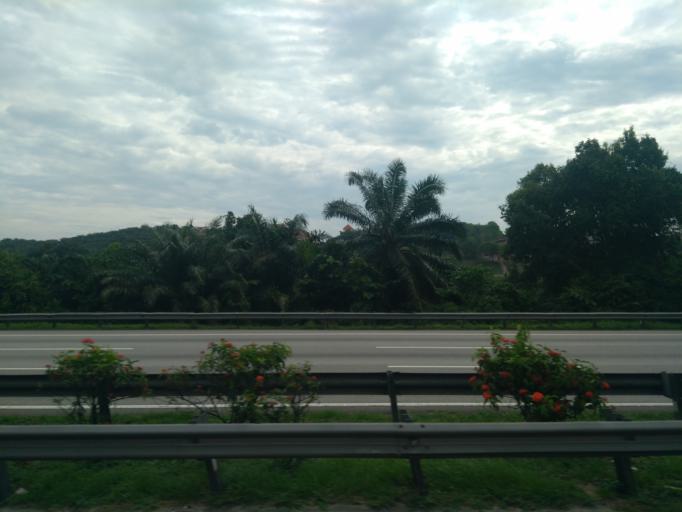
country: MY
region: Negeri Sembilan
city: Seremban
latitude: 2.6462
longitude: 101.9927
